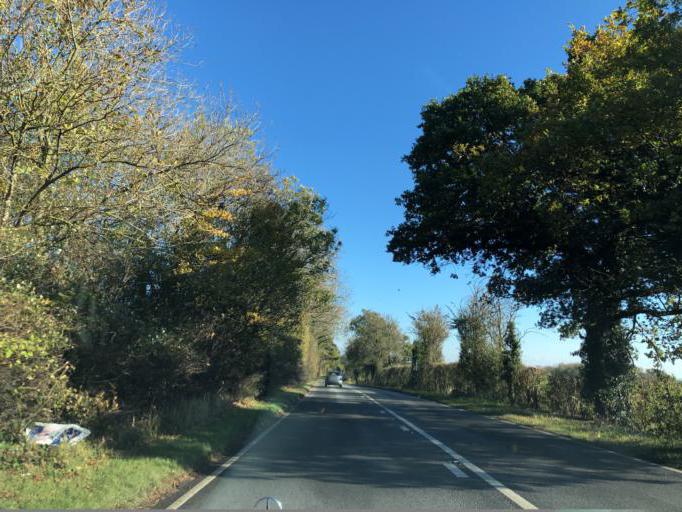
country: GB
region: England
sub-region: Warwickshire
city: Harbury
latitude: 52.2542
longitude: -1.4299
